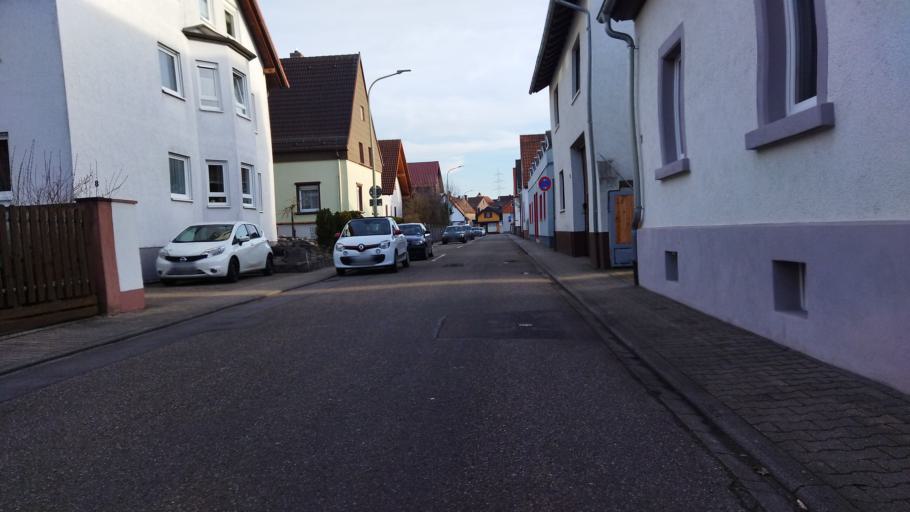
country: DE
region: Rheinland-Pfalz
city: Worth am Rhein
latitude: 49.0527
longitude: 8.2648
